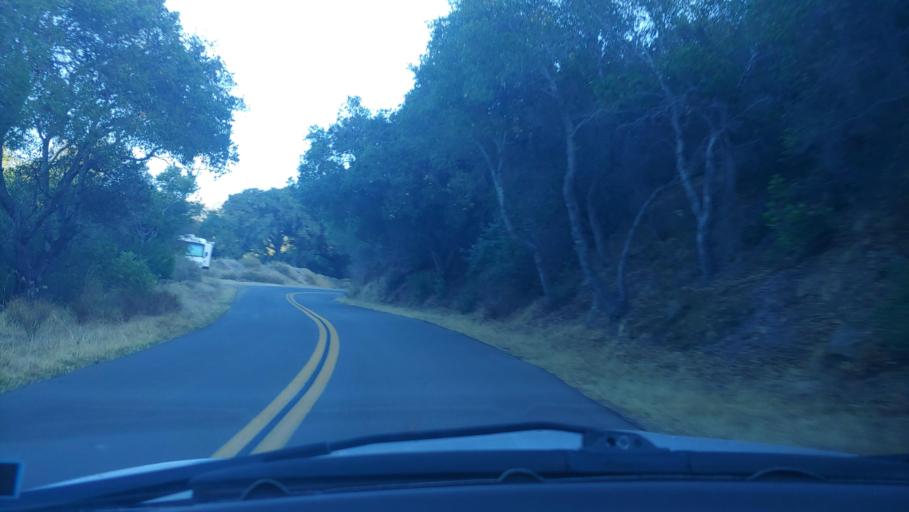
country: US
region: California
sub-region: Santa Barbara County
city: Goleta
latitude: 34.5338
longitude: -119.8420
